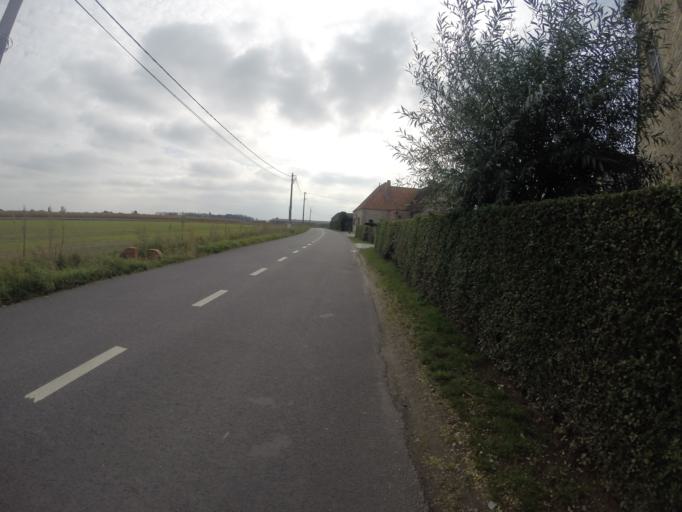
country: BE
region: Flanders
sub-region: Provincie Oost-Vlaanderen
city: Aalter
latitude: 51.0786
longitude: 3.4274
